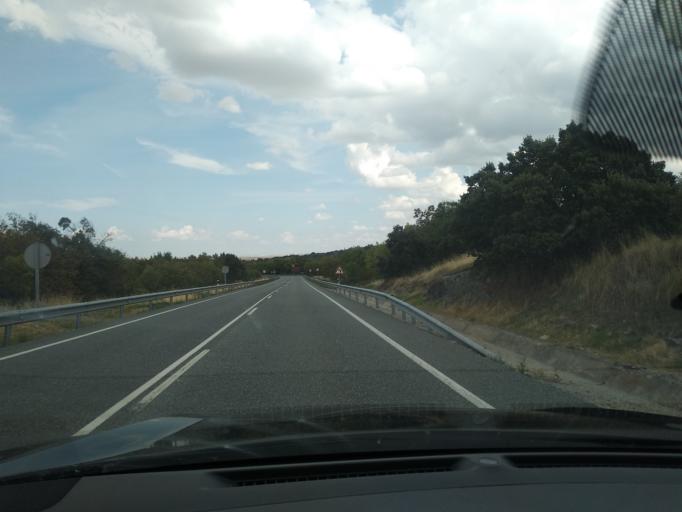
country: ES
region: Castille and Leon
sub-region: Provincia de Segovia
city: Palazuelos de Eresma
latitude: 40.8754
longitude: -4.1000
